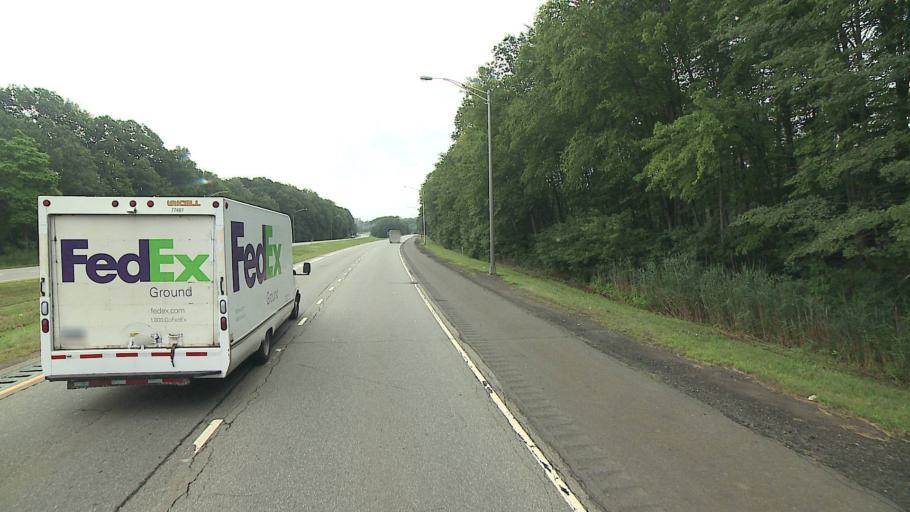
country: US
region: Connecticut
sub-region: New Haven County
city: Wallingford Center
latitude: 41.4272
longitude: -72.8316
